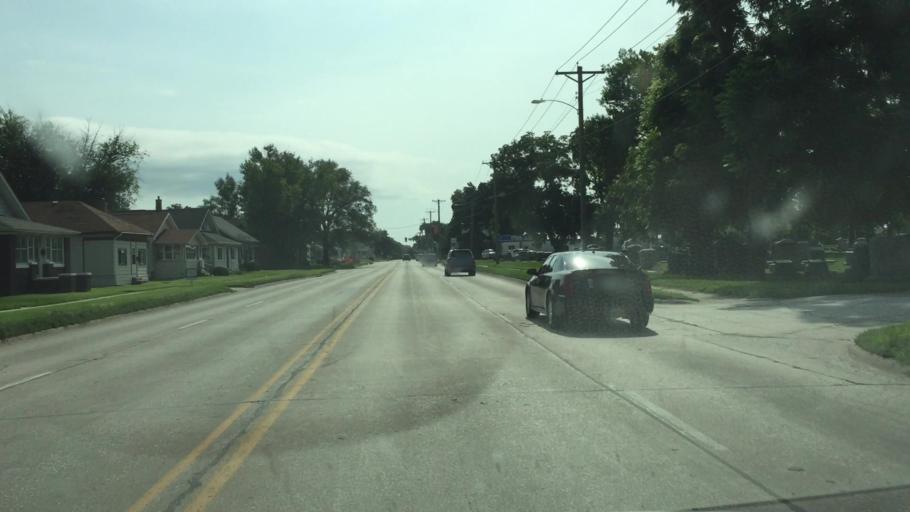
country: US
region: Iowa
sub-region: Lee County
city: Fort Madison
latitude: 40.6272
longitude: -91.3365
